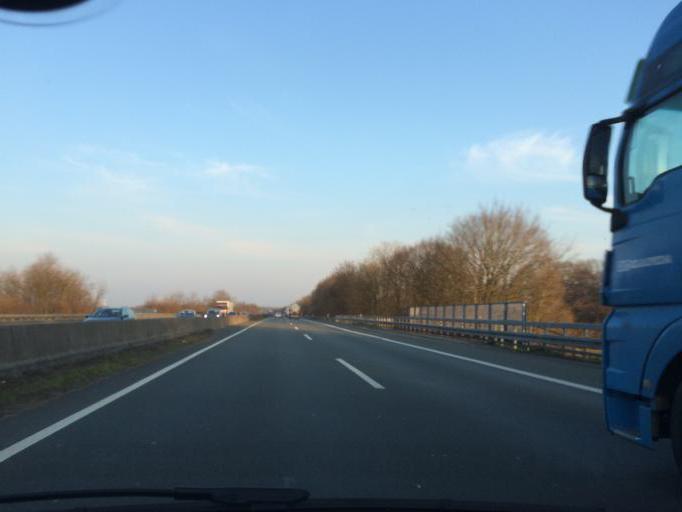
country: DE
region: North Rhine-Westphalia
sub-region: Regierungsbezirk Munster
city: Senden
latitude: 51.9024
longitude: 7.4609
